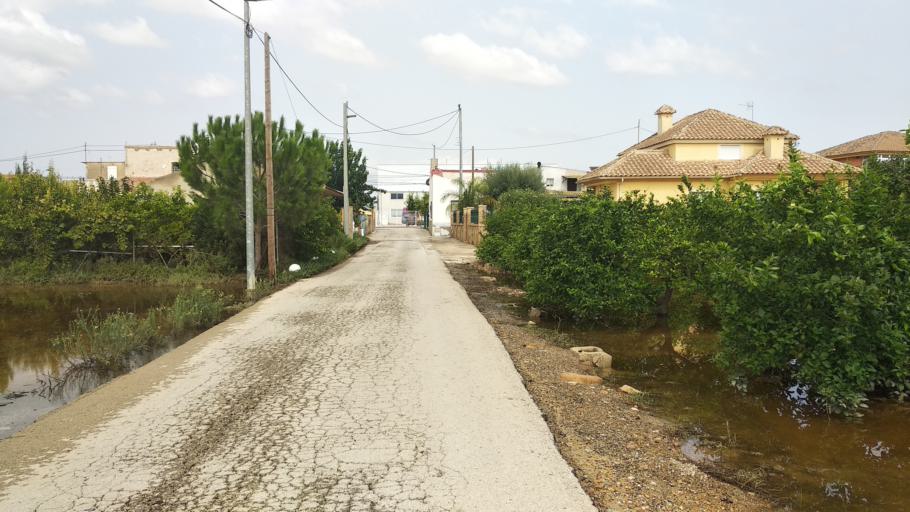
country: ES
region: Murcia
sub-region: Murcia
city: Santomera
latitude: 38.0422
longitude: -1.0416
